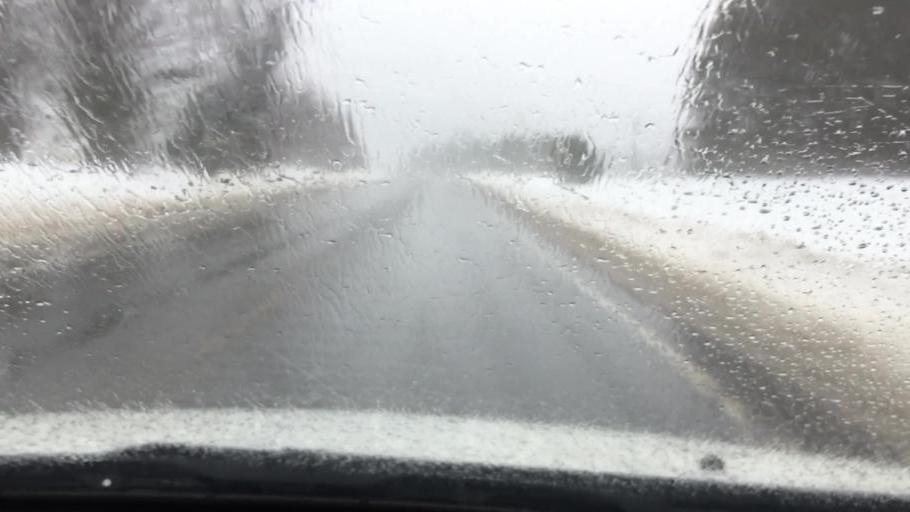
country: US
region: Michigan
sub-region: Antrim County
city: Mancelona
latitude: 44.9440
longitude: -85.0506
